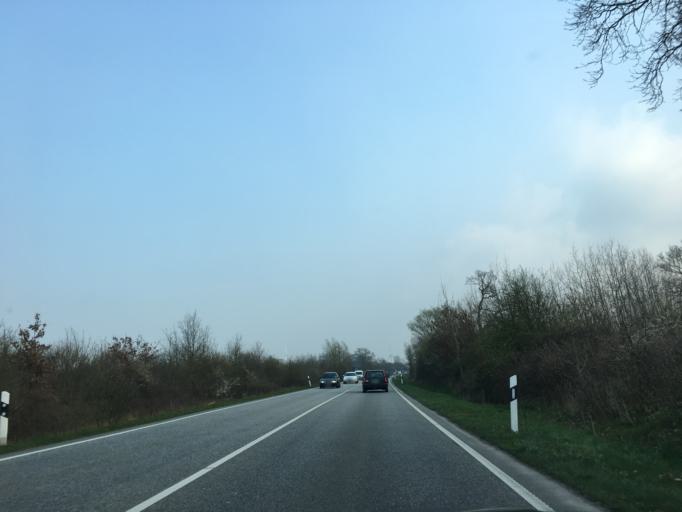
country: DE
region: Schleswig-Holstein
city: Tuttendorf
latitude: 54.4123
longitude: 9.9944
